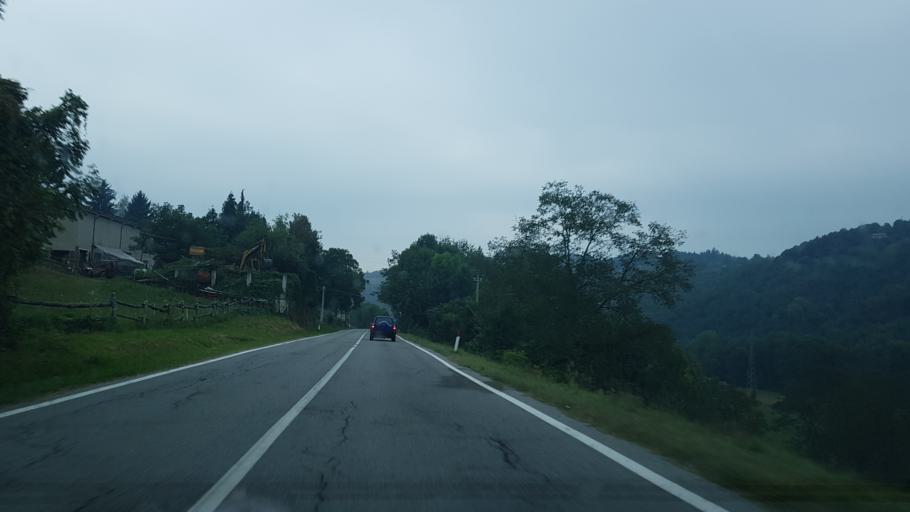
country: IT
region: Piedmont
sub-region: Provincia di Cuneo
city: Frabosa Sottana
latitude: 44.3143
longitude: 7.8038
